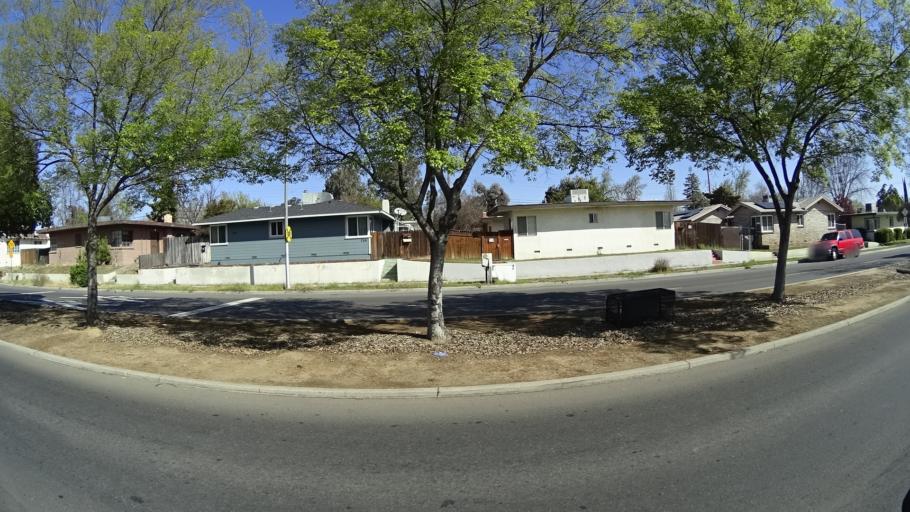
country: US
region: California
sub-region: Fresno County
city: Fresno
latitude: 36.7793
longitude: -119.8012
